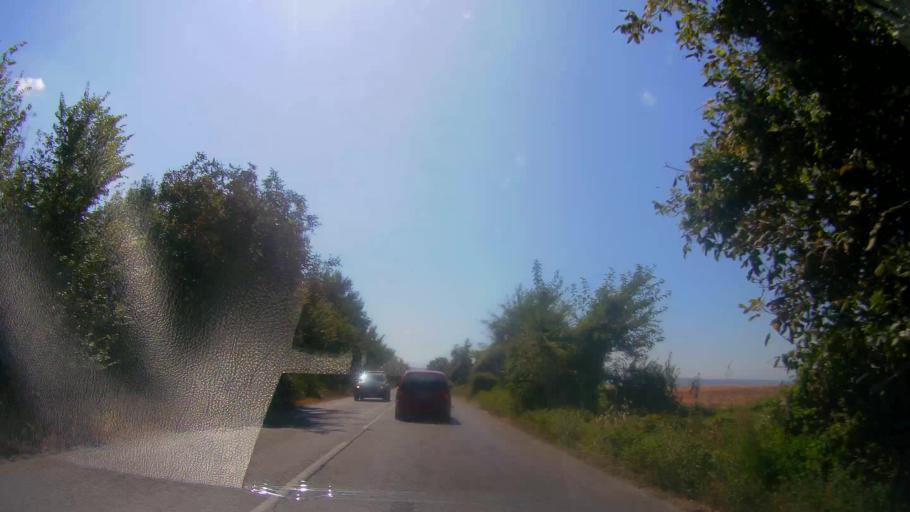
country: BG
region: Veliko Turnovo
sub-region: Obshtina Gorna Oryakhovitsa
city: Purvomaytsi
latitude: 43.2340
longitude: 25.6404
